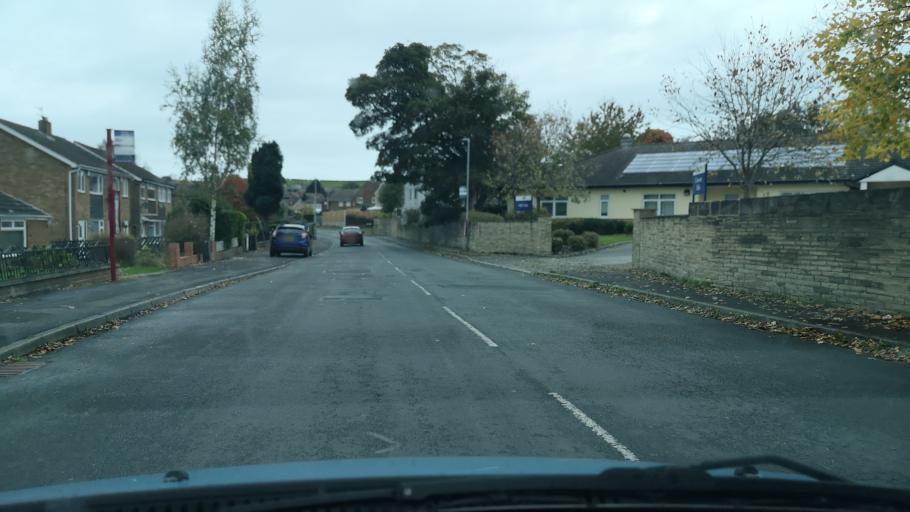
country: GB
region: England
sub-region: Kirklees
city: Heckmondwike
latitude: 53.7137
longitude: -1.6738
